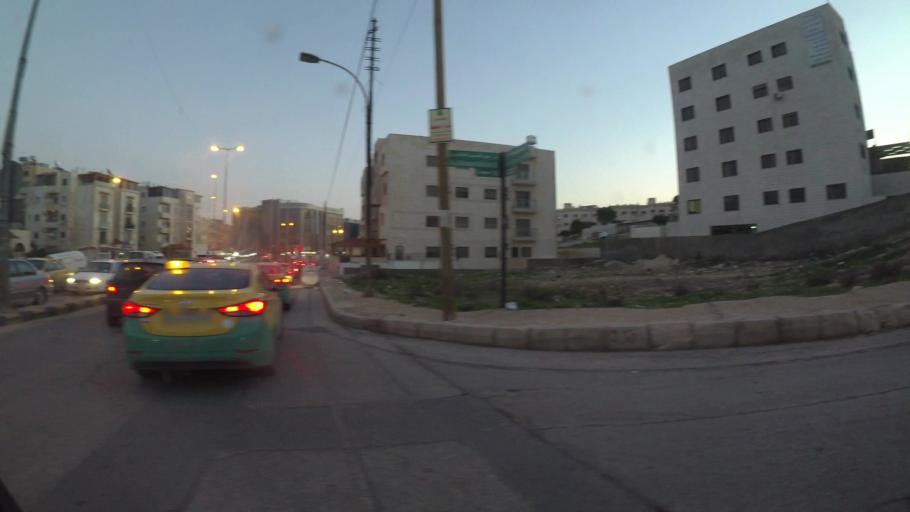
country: JO
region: Amman
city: Al Jubayhah
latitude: 31.9959
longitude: 35.8596
